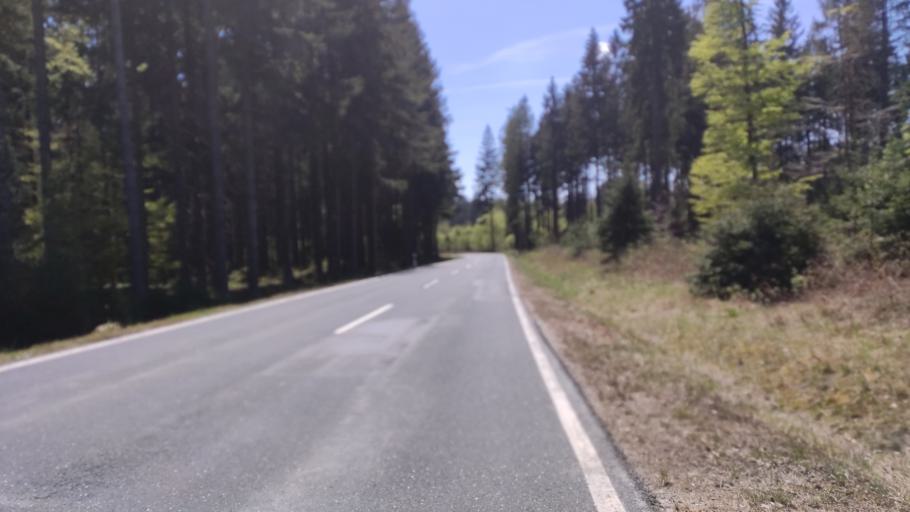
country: DE
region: Bavaria
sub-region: Upper Franconia
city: Tschirn
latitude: 50.3745
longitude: 11.4510
